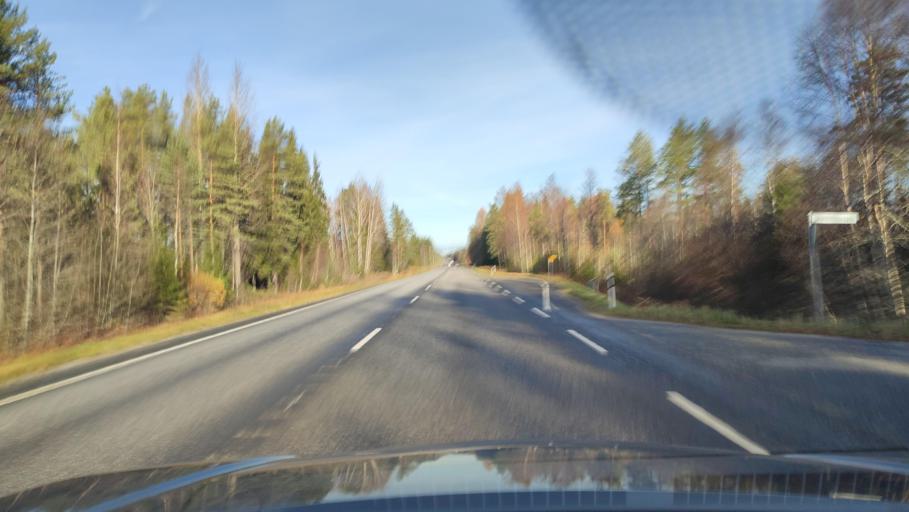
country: FI
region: Ostrobothnia
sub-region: Vaasa
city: Malax
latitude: 62.8012
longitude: 21.6768
